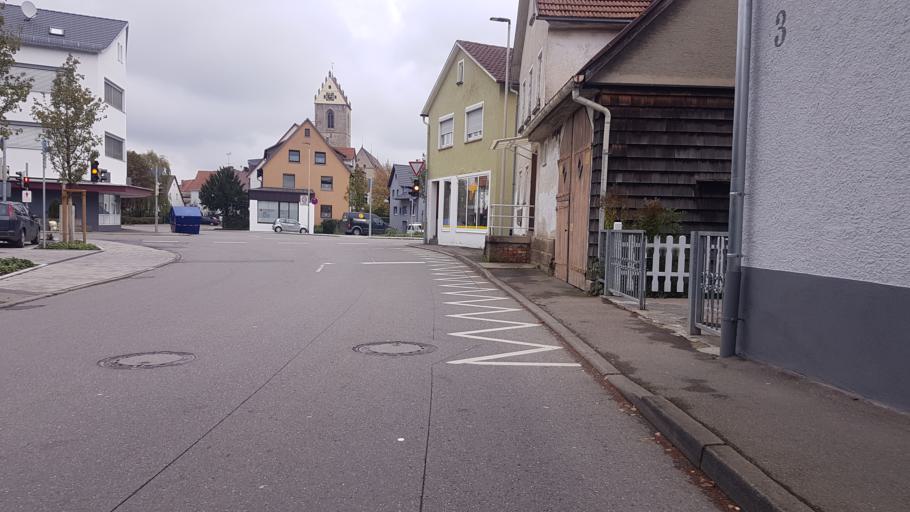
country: DE
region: Baden-Wuerttemberg
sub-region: Tuebingen Region
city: Ofterdingen
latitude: 48.4196
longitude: 9.0325
